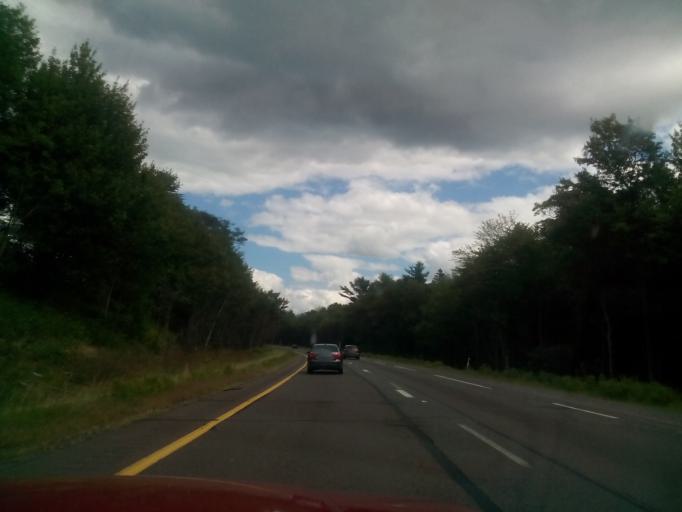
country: US
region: Pennsylvania
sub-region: Monroe County
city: Pocono Pines
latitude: 41.0730
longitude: -75.4972
